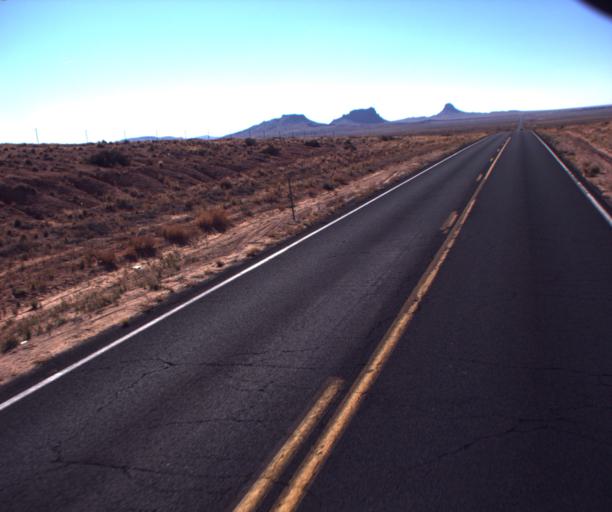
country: US
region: Arizona
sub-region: Navajo County
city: Dilkon
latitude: 35.3945
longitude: -110.4259
